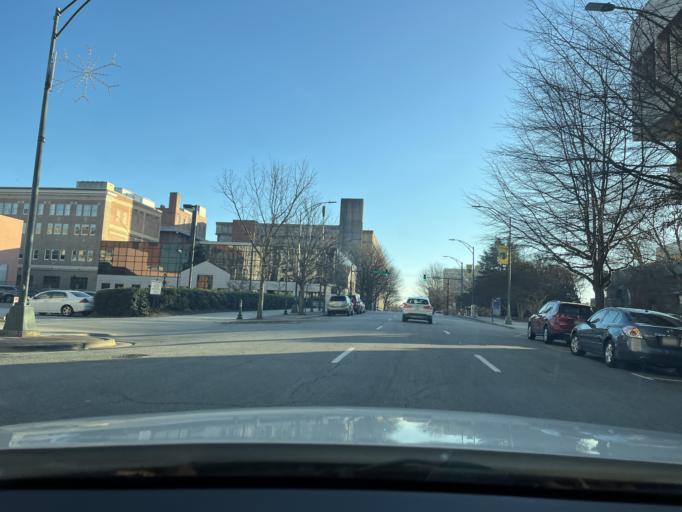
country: US
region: North Carolina
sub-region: Guilford County
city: Greensboro
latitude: 36.0724
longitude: -79.7916
